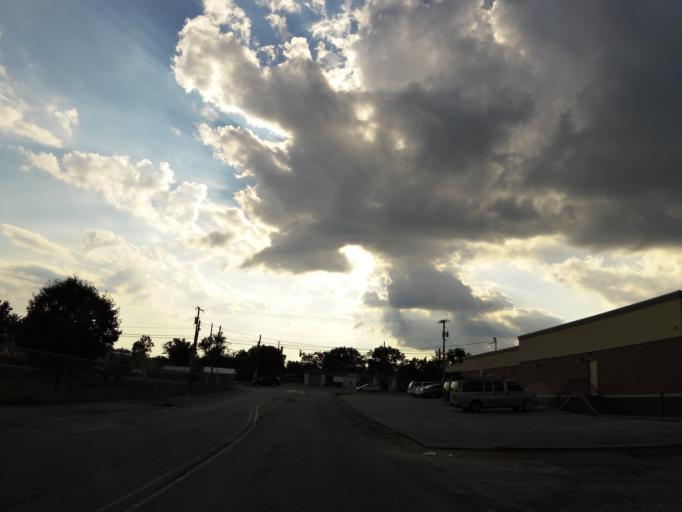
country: US
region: Tennessee
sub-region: Blount County
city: Eagleton Village
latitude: 35.7940
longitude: -83.9452
